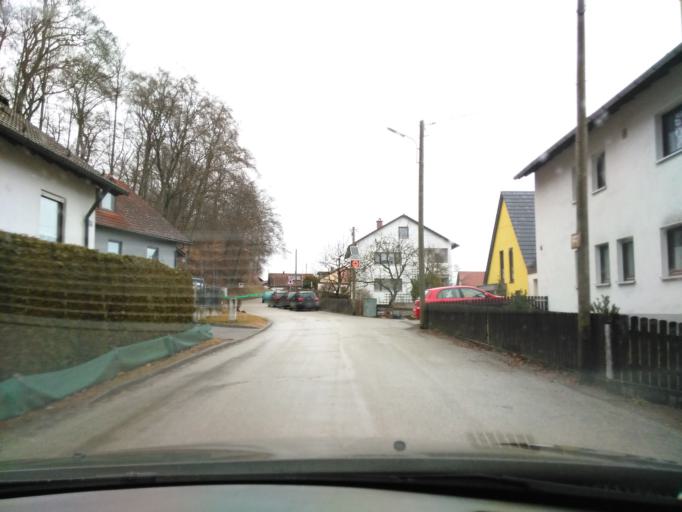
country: DE
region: Bavaria
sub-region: Upper Bavaria
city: Fuerstenfeldbruck
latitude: 48.1838
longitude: 11.2208
